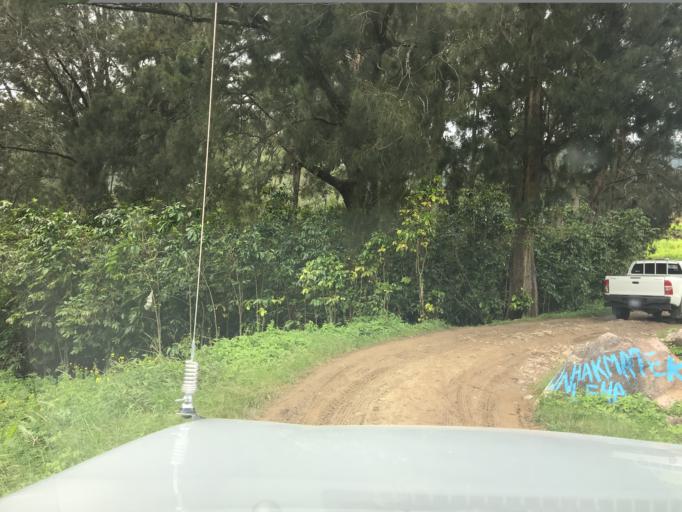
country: TL
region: Aileu
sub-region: Aileu Villa
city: Aileu
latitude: -8.8593
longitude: 125.5725
